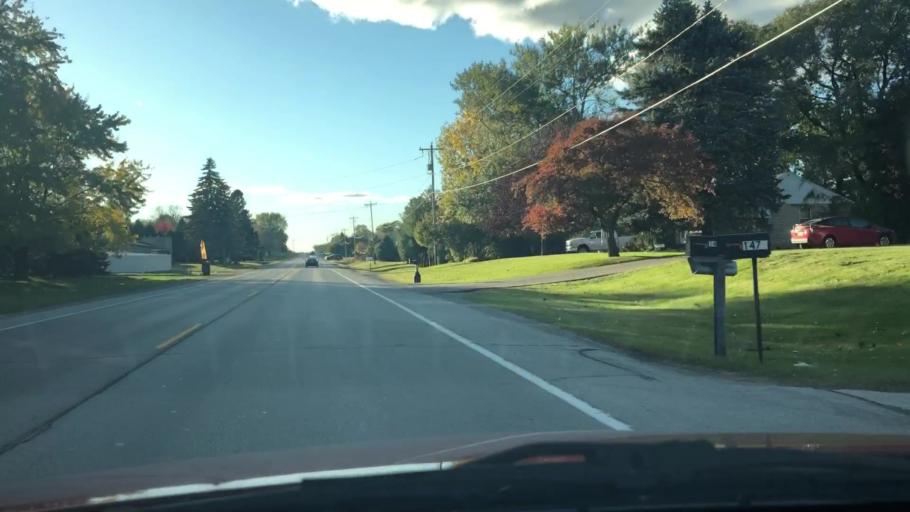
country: US
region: Wisconsin
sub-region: Brown County
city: De Pere
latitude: 44.4452
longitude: -88.1035
